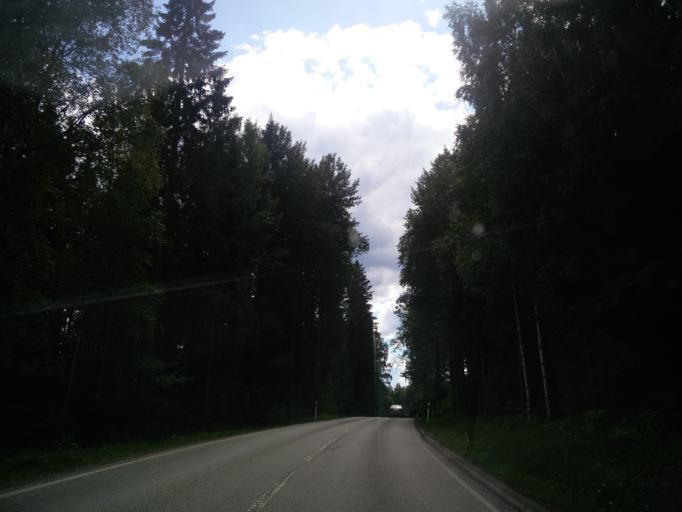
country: SE
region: OErebro
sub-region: Ljusnarsbergs Kommun
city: Kopparberg
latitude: 59.8559
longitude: 15.0006
